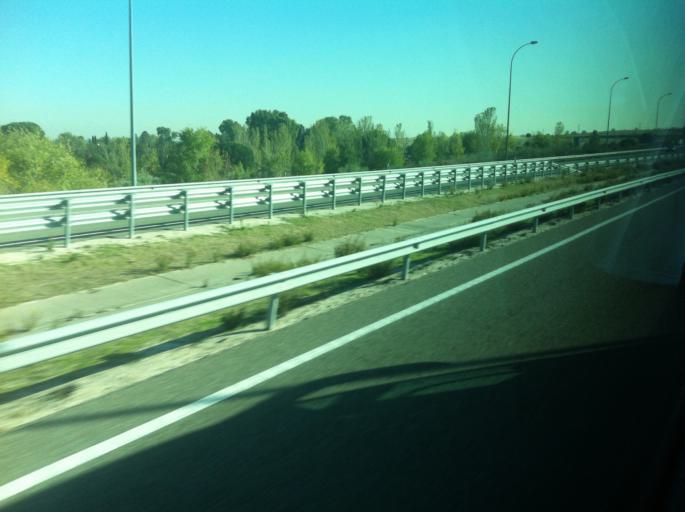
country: ES
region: Madrid
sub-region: Provincia de Madrid
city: San Sebastian de los Reyes
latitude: 40.5187
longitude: -3.5985
